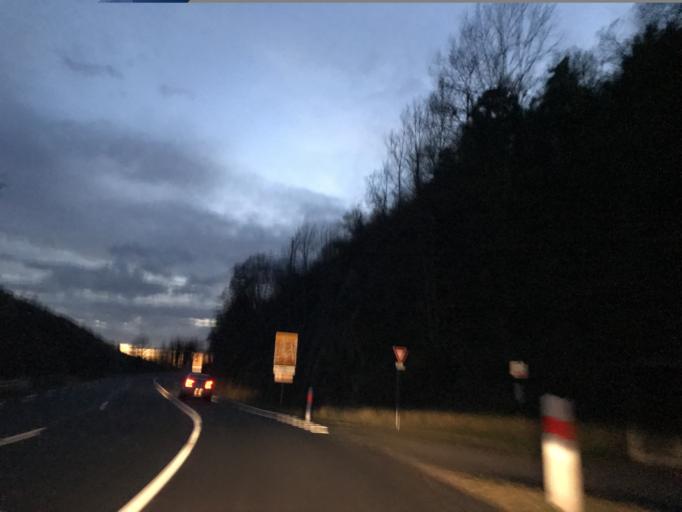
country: FR
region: Auvergne
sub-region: Departement du Puy-de-Dome
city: Thiers
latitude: 45.8655
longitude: 3.5621
